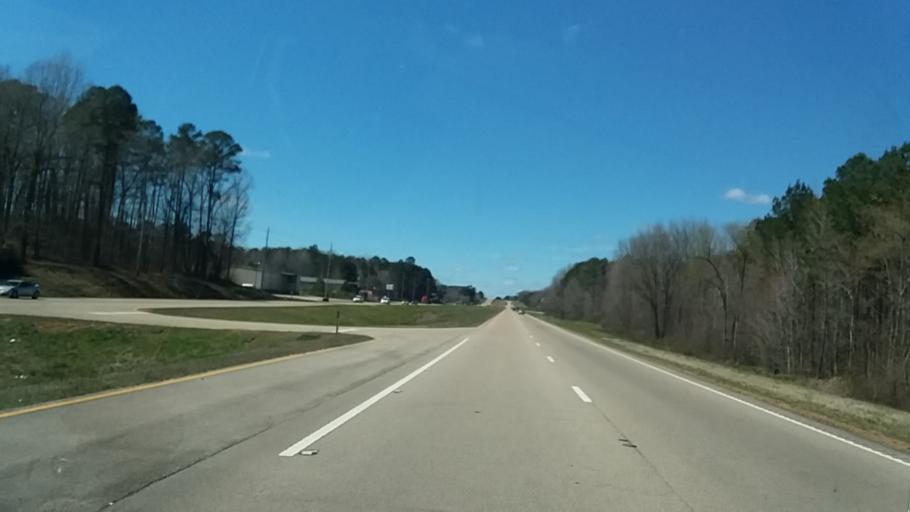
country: US
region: Mississippi
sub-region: Alcorn County
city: Farmington
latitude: 34.8697
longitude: -88.4250
